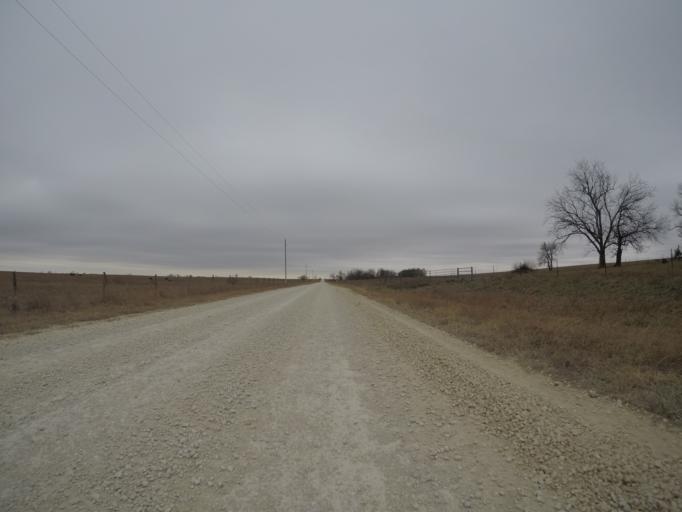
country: US
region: Kansas
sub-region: Wabaunsee County
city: Alma
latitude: 38.8338
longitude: -96.1133
